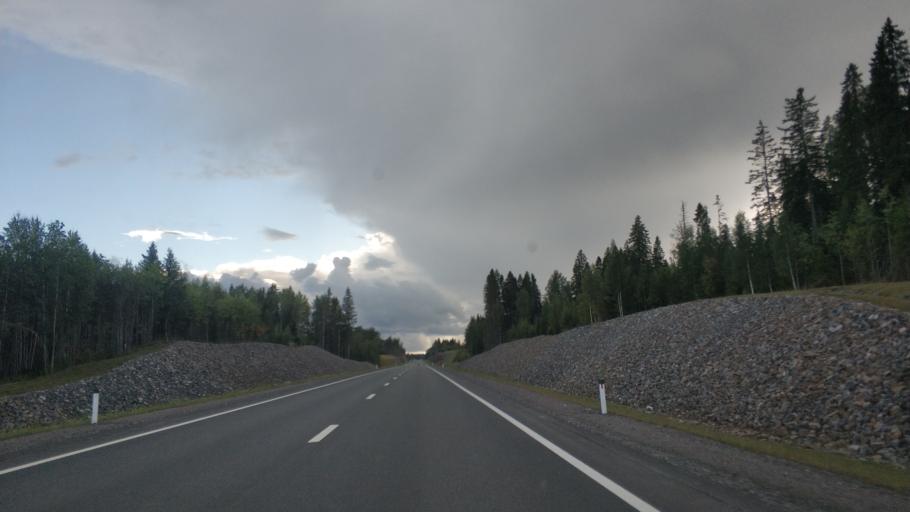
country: RU
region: Republic of Karelia
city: Lakhdenpokh'ya
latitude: 61.4417
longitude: 29.9856
